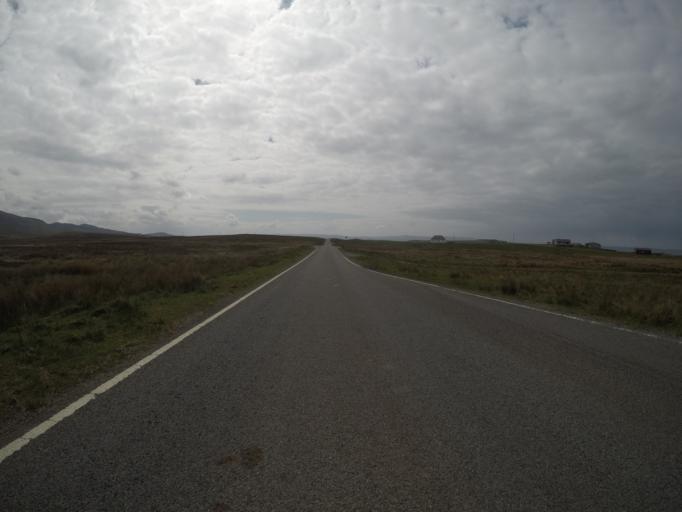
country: GB
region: Scotland
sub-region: Highland
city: Portree
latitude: 57.6567
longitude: -6.3757
